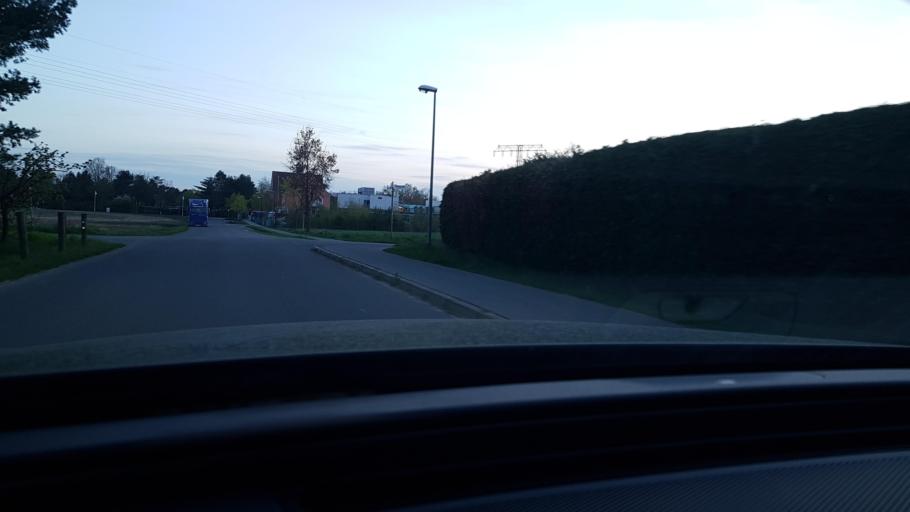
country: DE
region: Berlin
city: Lichtenrade
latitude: 52.3505
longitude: 13.4260
